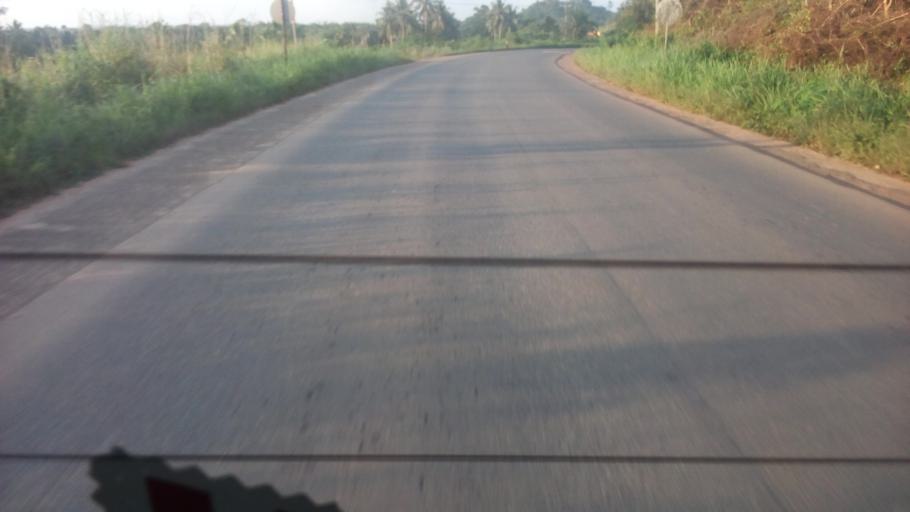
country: GH
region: Western
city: Tarkwa
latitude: 5.1603
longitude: -2.0745
